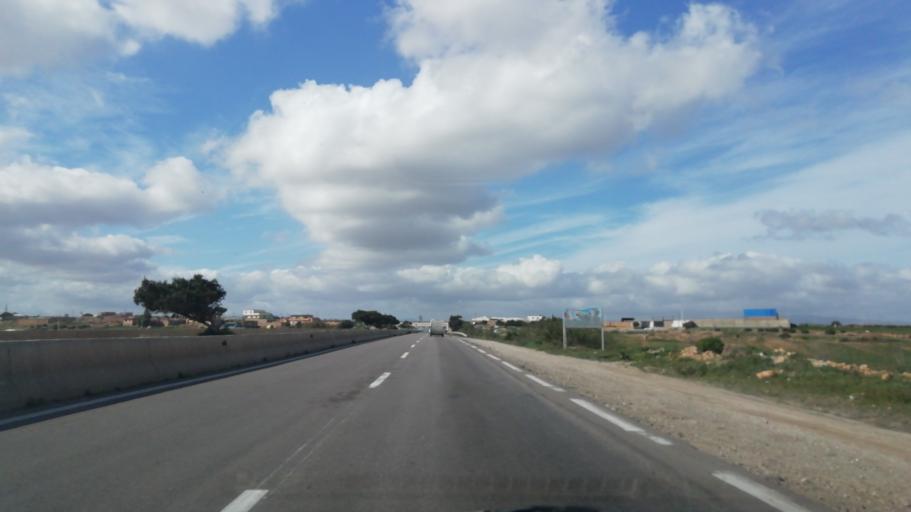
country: DZ
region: Oran
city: Ain el Bya
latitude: 35.7670
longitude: -0.2161
